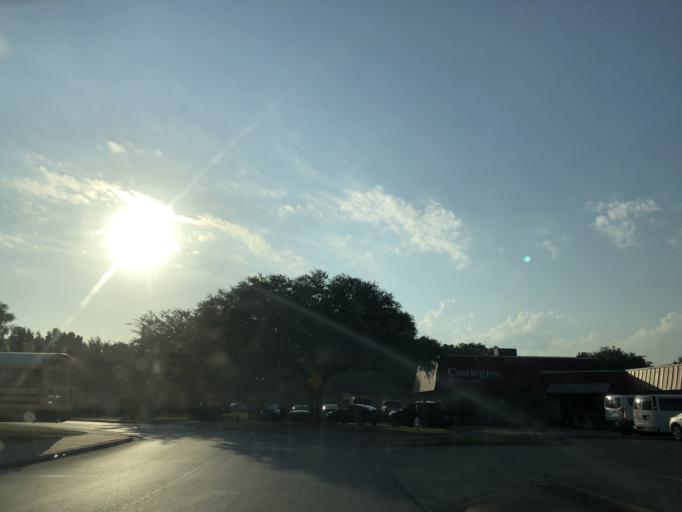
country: US
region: Texas
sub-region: Dallas County
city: Sunnyvale
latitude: 32.8452
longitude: -96.5941
